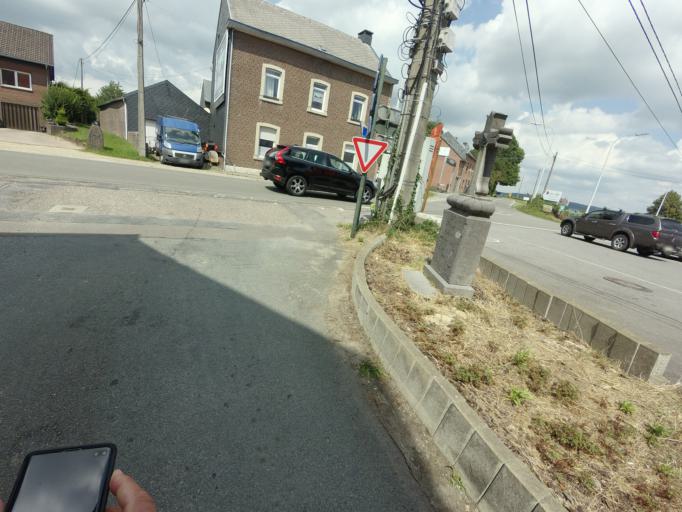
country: BE
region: Wallonia
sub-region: Province de Liege
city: Lontzen
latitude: 50.7024
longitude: 5.9818
